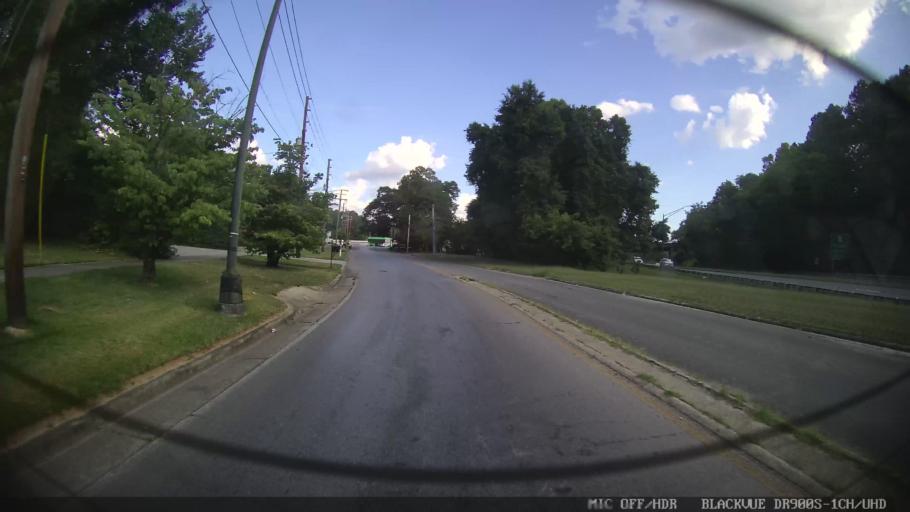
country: US
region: Georgia
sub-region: Floyd County
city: Rome
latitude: 34.2388
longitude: -85.1608
